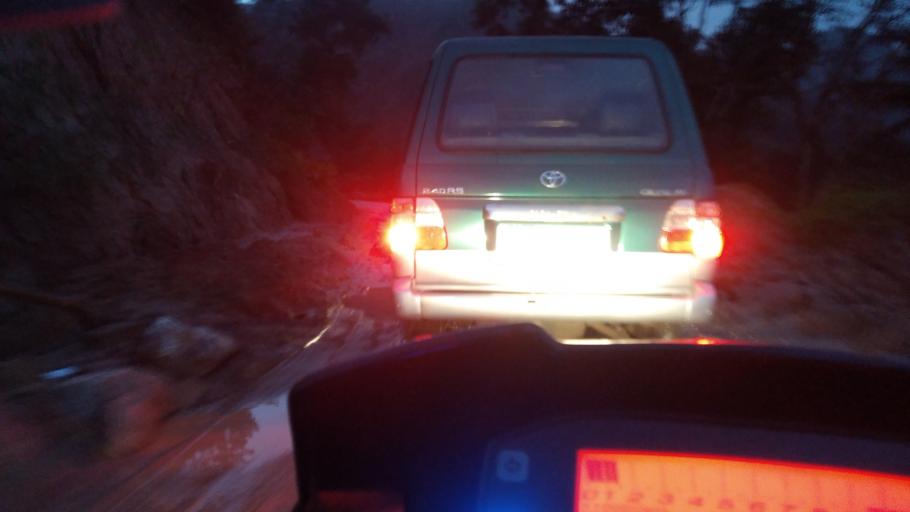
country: IN
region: Kerala
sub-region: Idukki
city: Munnar
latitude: 9.9766
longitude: 77.0579
